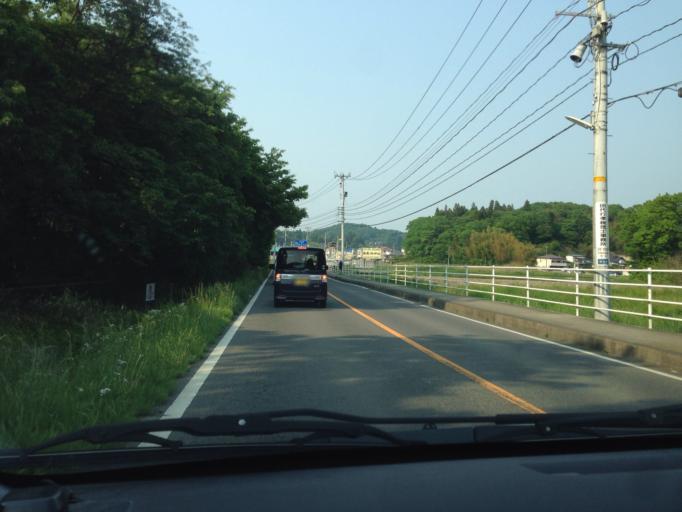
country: JP
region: Tochigi
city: Kuroiso
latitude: 37.1109
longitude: 140.1974
